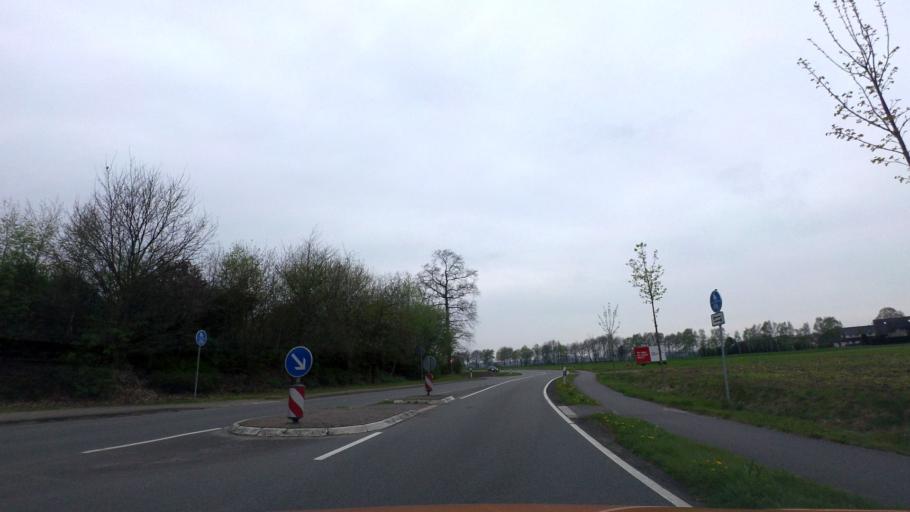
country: DE
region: Lower Saxony
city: Neuenkirchen
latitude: 52.4980
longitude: 8.0689
